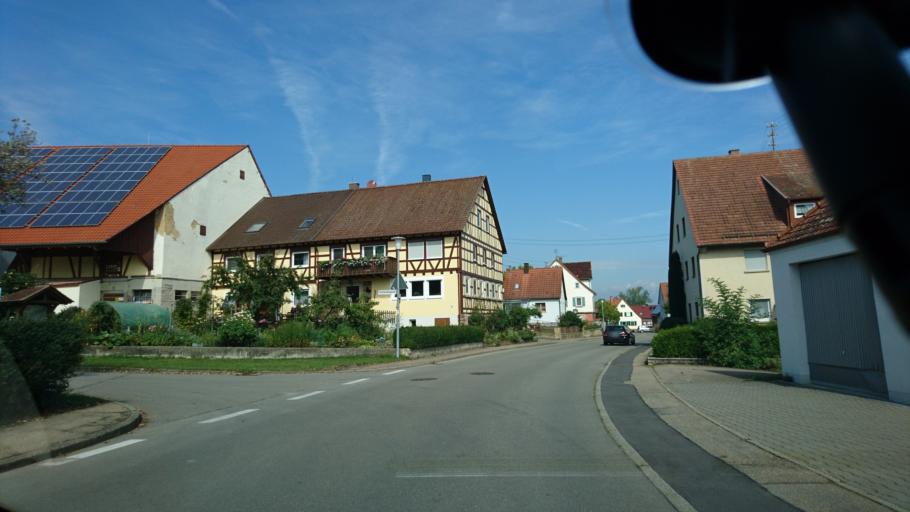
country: DE
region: Baden-Wuerttemberg
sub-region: Regierungsbezirk Stuttgart
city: Ilshofen
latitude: 49.1538
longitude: 9.9302
